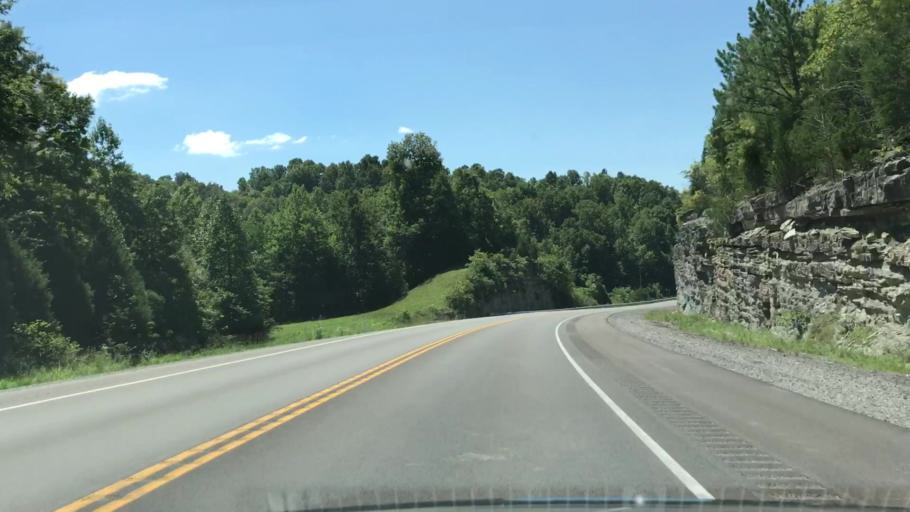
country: US
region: Kentucky
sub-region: Cumberland County
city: Burkesville
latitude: 36.7125
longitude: -85.3640
